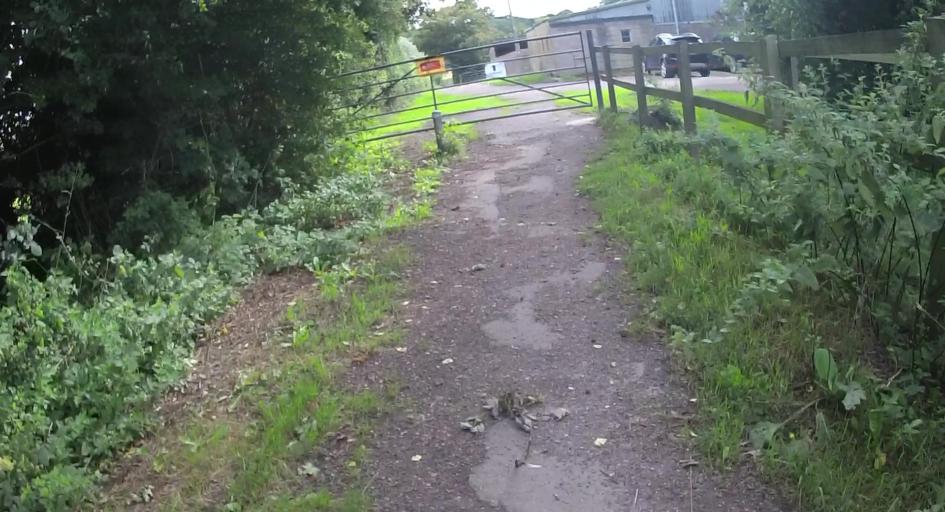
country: GB
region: England
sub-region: West Berkshire
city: Thatcham
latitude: 51.3896
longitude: -1.2392
